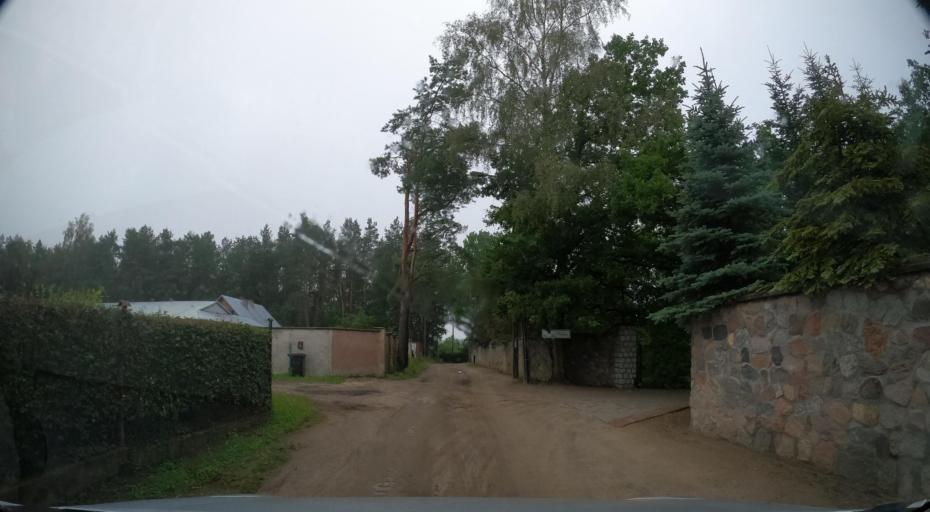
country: PL
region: Pomeranian Voivodeship
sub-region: Powiat kartuski
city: Chwaszczyno
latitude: 54.4353
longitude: 18.4146
